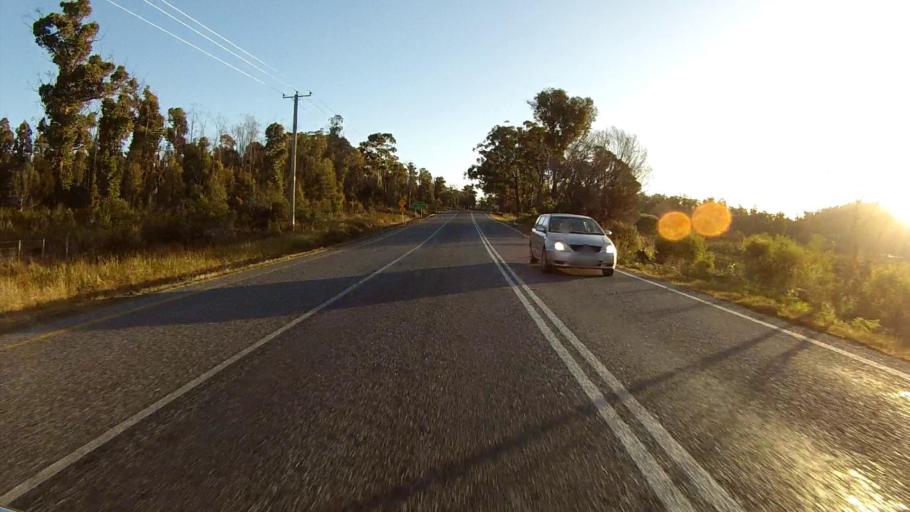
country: AU
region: Tasmania
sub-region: Sorell
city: Sorell
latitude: -42.8223
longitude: 147.6869
